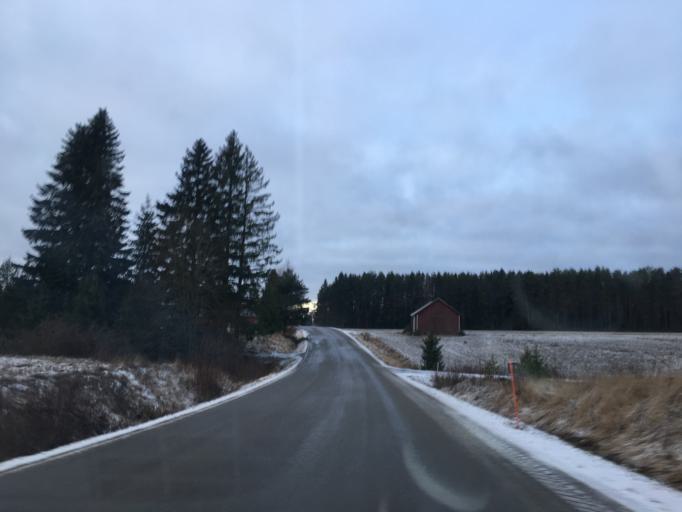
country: FI
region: Varsinais-Suomi
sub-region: Turku
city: Lieto
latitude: 60.5808
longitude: 22.5084
